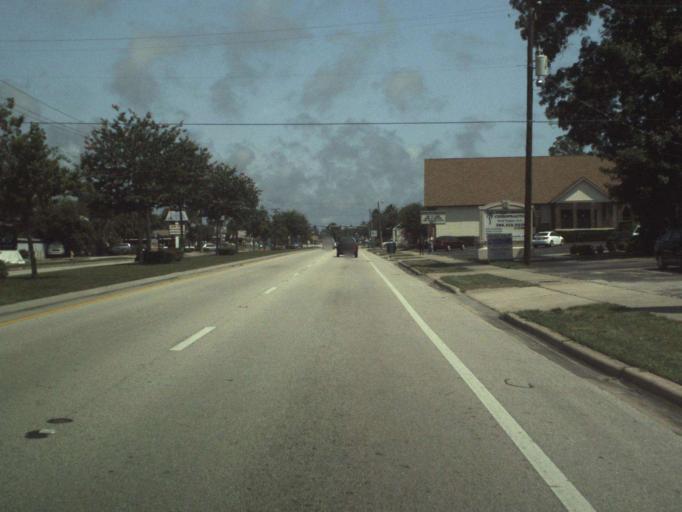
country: US
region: Florida
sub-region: Volusia County
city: Holly Hill
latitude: 29.2590
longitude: -81.0486
